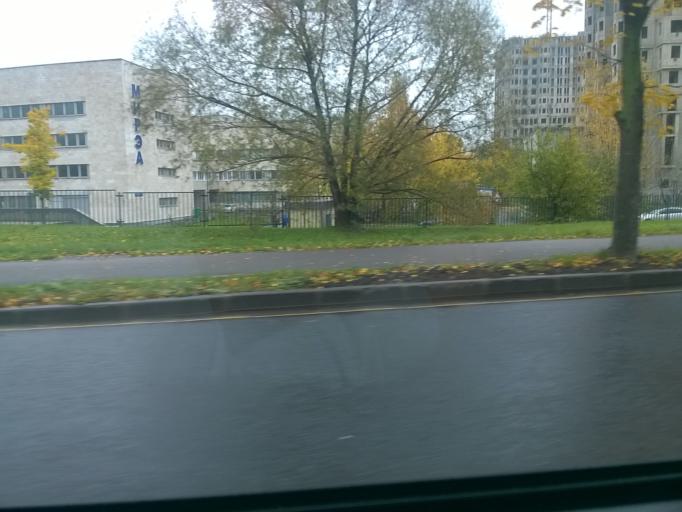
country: RU
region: Moscow
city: Troparevo
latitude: 55.6678
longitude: 37.4799
